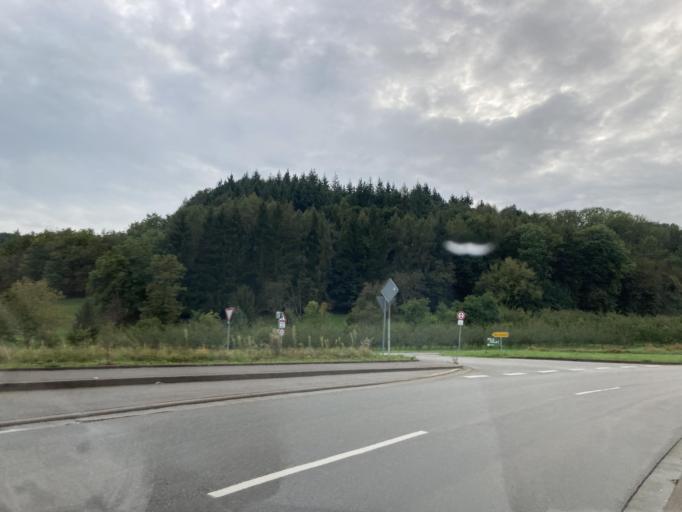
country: DE
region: Baden-Wuerttemberg
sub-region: Freiburg Region
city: Feldberg
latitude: 47.7729
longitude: 7.6298
